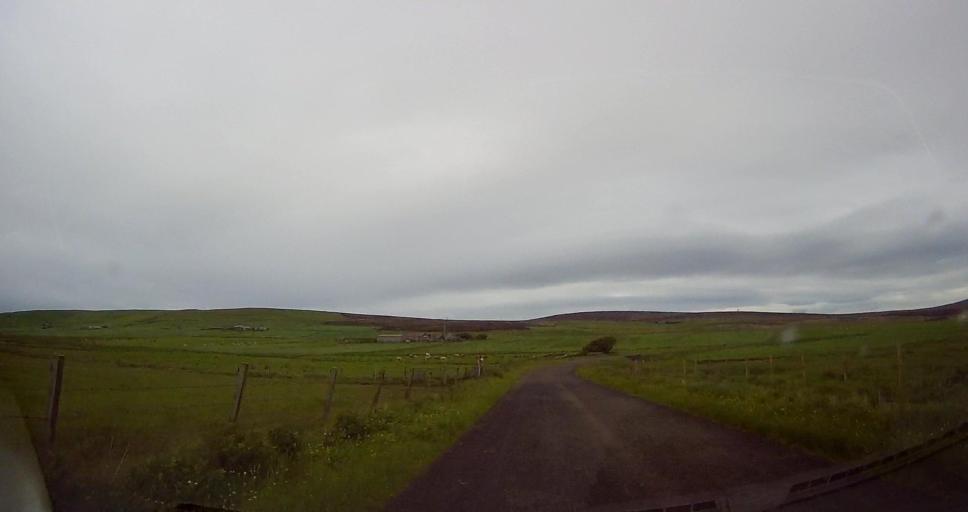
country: GB
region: Scotland
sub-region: Orkney Islands
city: Stromness
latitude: 59.0843
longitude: -3.1900
